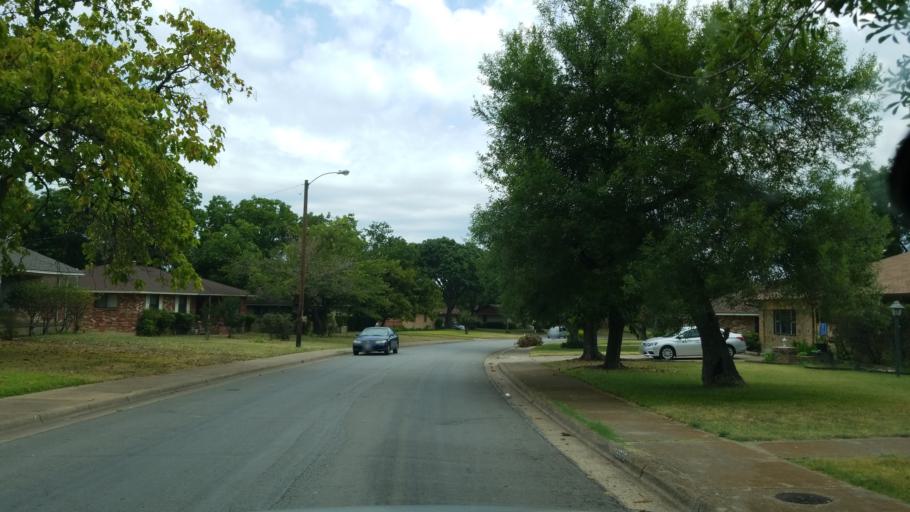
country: US
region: Texas
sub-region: Dallas County
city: Duncanville
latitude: 32.6635
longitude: -96.8383
